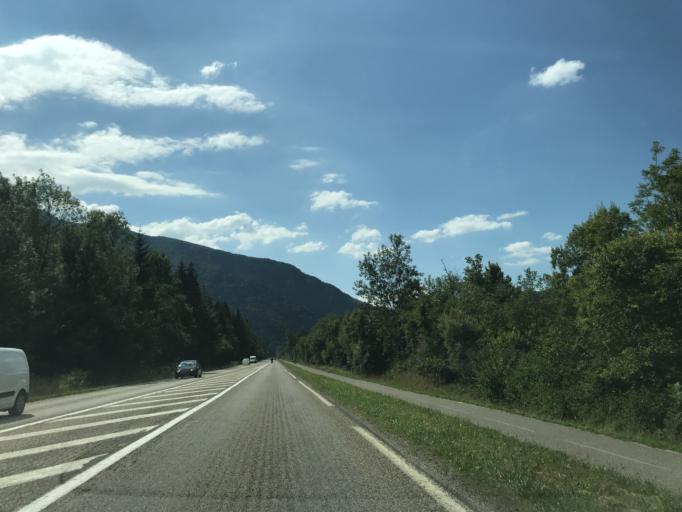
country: FR
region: Rhone-Alpes
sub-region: Departement de la Haute-Savoie
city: Dingy-Saint-Clair
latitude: 45.8951
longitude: 6.2369
